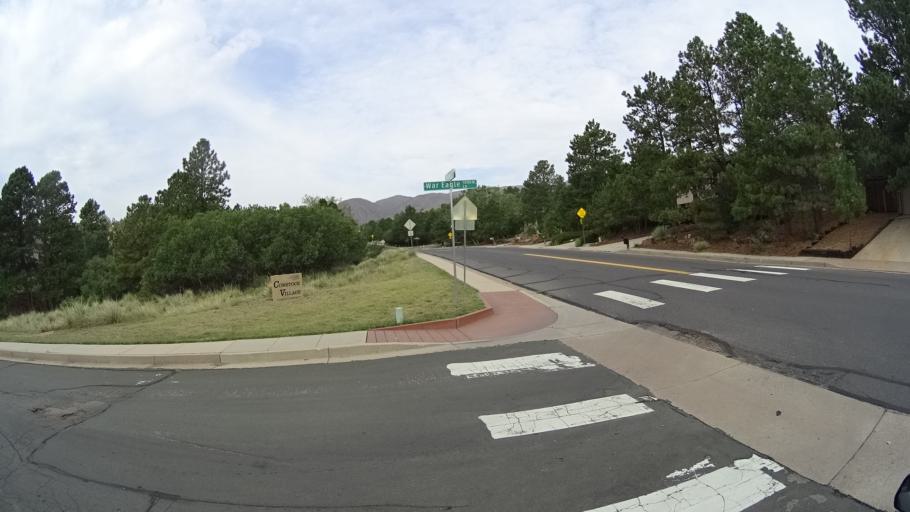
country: US
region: Colorado
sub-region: El Paso County
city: Air Force Academy
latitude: 38.9298
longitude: -104.8476
